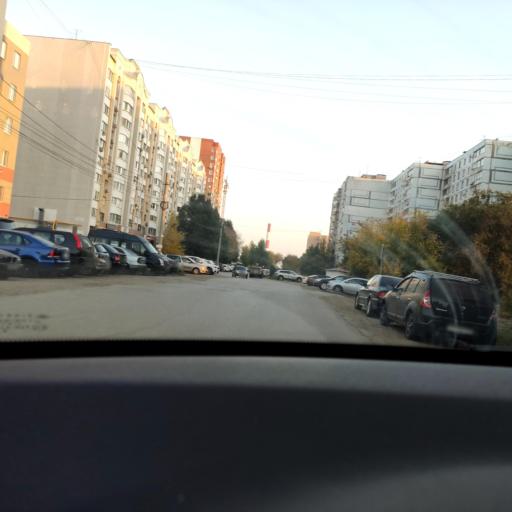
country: RU
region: Samara
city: Samara
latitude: 53.1984
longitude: 50.1444
